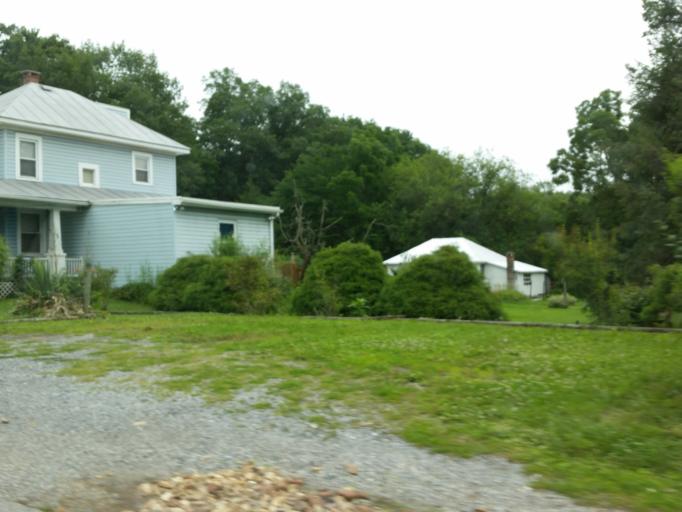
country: US
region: Pennsylvania
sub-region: York County
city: Emigsville
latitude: 40.0068
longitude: -76.7496
